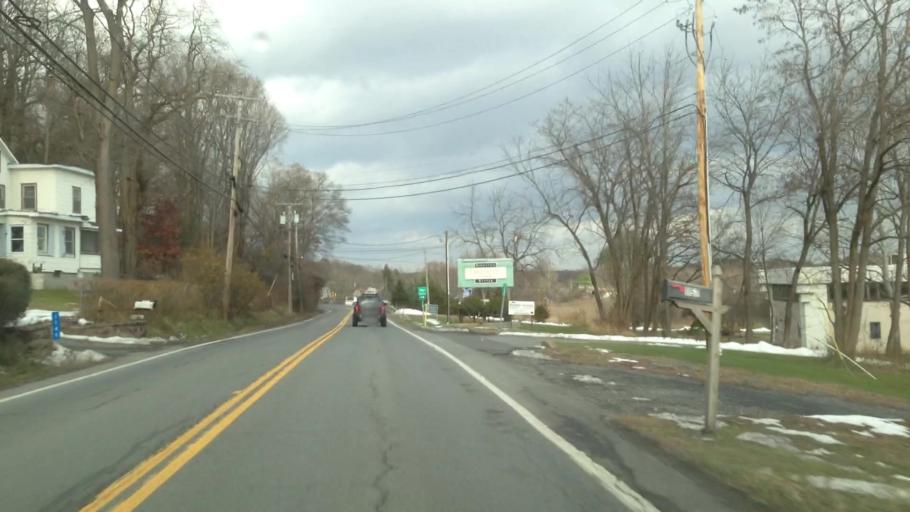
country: US
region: New York
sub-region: Ulster County
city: Lake Katrine
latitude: 41.9856
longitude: -73.9691
